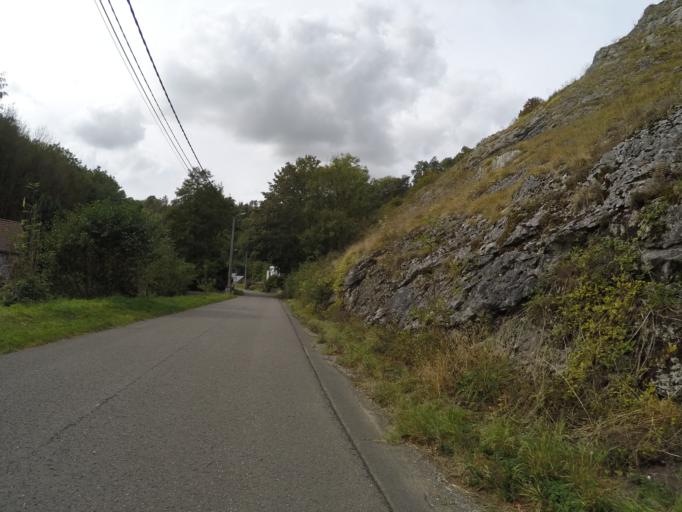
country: BE
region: Wallonia
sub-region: Province de Namur
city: Dinant
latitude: 50.2735
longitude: 4.9226
